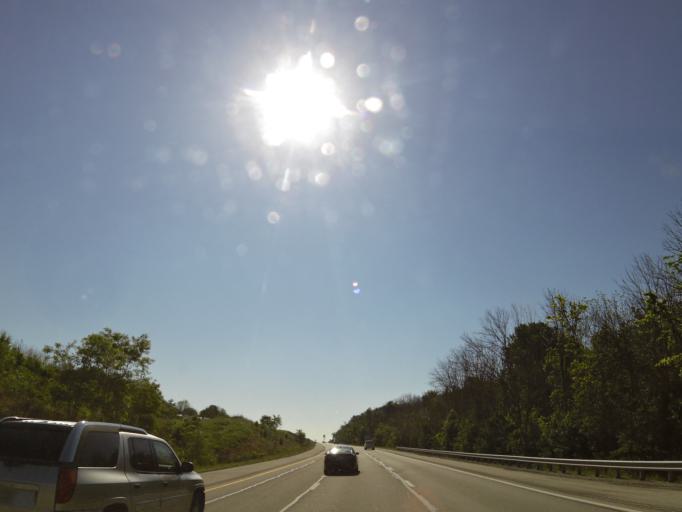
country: US
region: Kentucky
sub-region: Shelby County
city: Shelbyville
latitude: 38.1571
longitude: -85.0878
